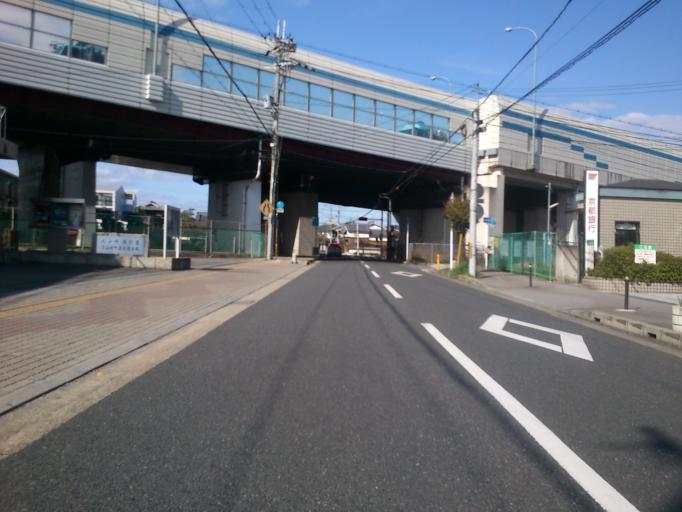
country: JP
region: Kyoto
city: Yawata
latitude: 34.9029
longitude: 135.6882
